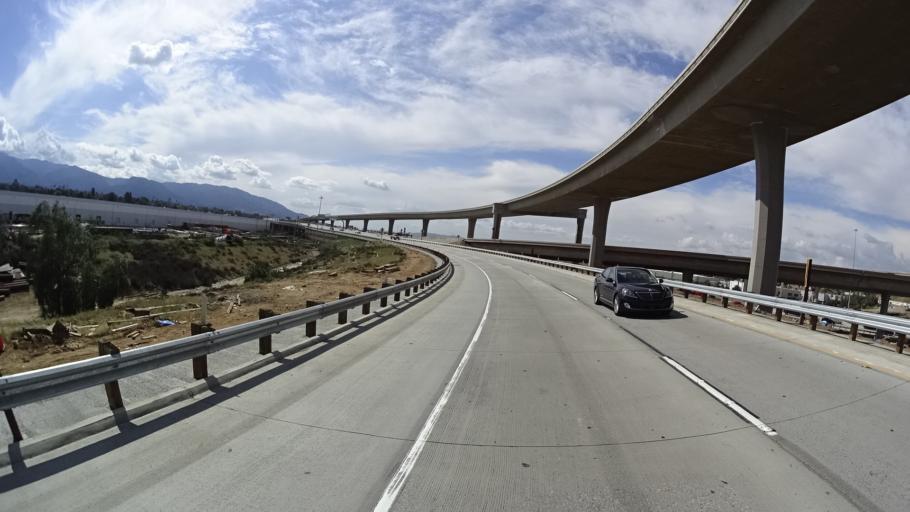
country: US
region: California
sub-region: Riverside County
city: Corona
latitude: 33.8806
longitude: -117.5483
